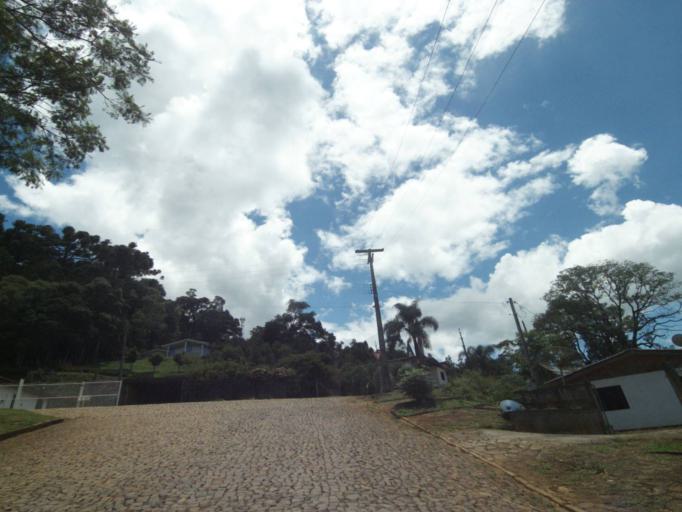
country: BR
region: Parana
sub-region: Uniao Da Vitoria
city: Uniao da Vitoria
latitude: -26.1607
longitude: -51.5563
